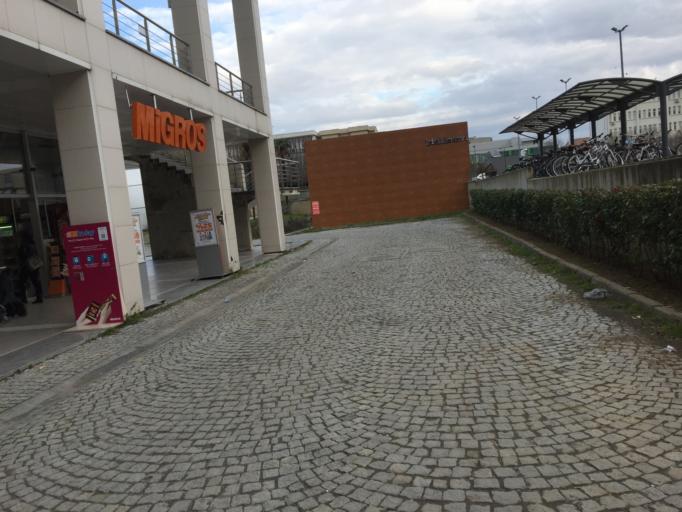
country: TR
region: Istanbul
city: Sisli
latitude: 41.1030
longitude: 29.0223
